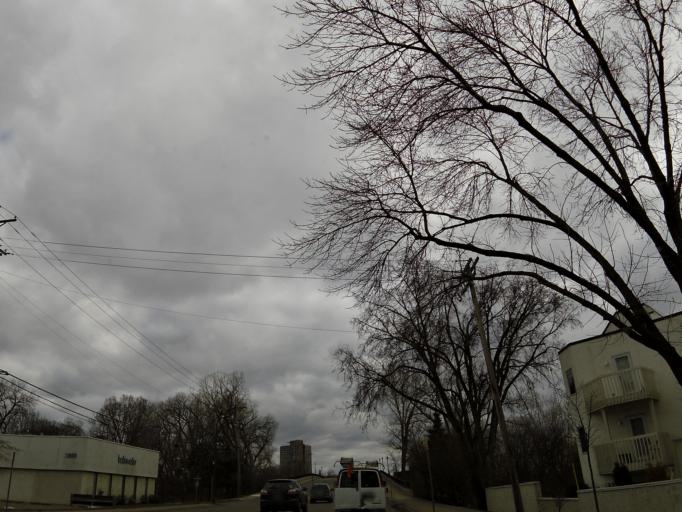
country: US
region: Minnesota
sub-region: Hennepin County
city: Saint Louis Park
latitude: 44.9484
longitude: -93.3259
